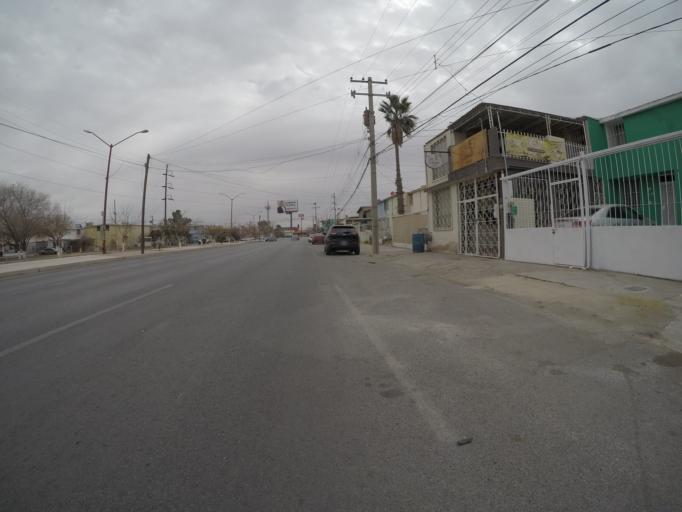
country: MX
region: Chihuahua
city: Ciudad Juarez
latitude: 31.7369
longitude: -106.4183
